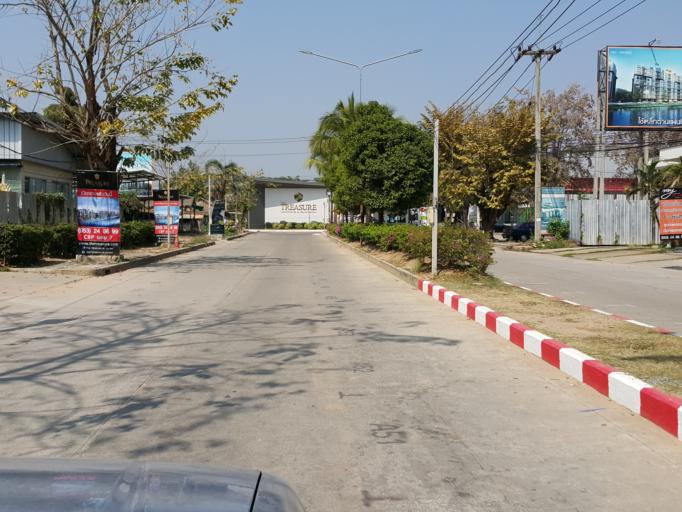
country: TH
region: Chiang Mai
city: Chiang Mai
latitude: 18.7999
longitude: 99.0233
